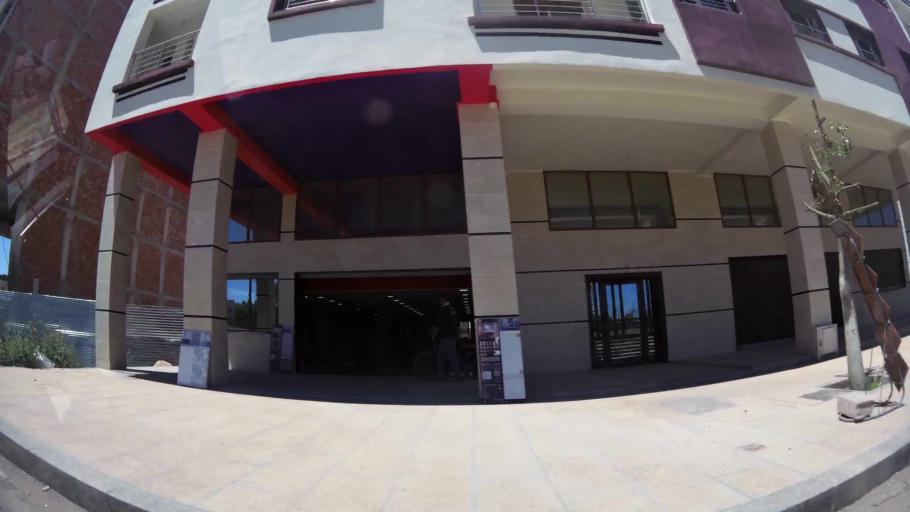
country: MA
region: Oriental
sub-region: Oujda-Angad
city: Oujda
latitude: 34.6698
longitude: -1.8757
